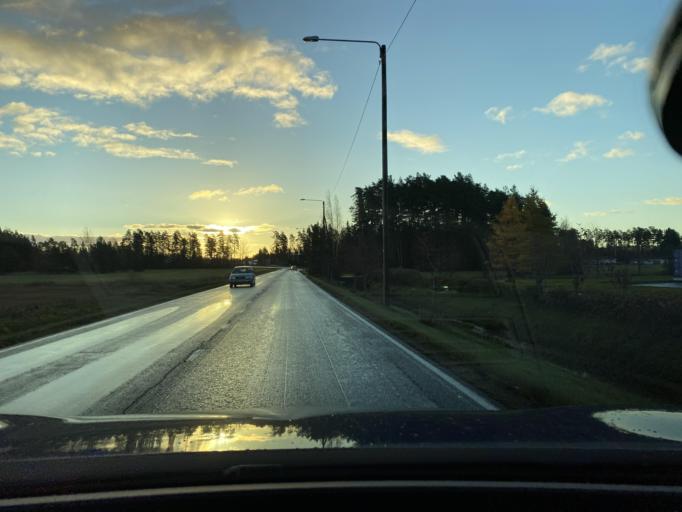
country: FI
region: Varsinais-Suomi
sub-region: Loimaa
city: Aura
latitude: 60.7242
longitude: 22.5859
